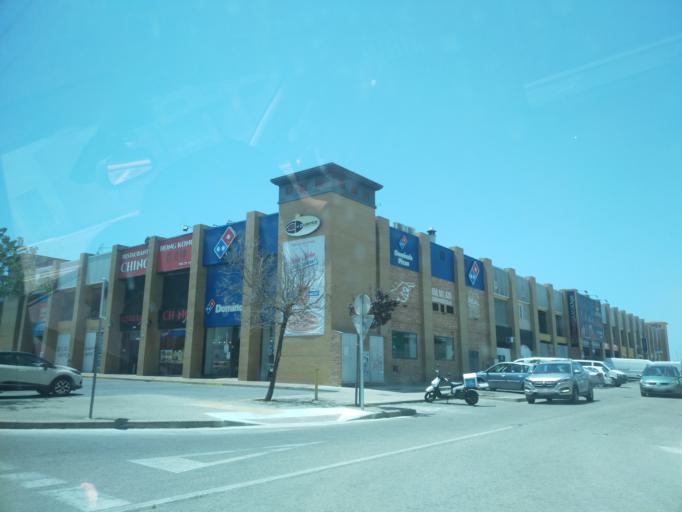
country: ES
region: Andalusia
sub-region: Provincia de Cadiz
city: Chiclana de la Frontera
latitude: 36.4264
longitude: -6.1524
